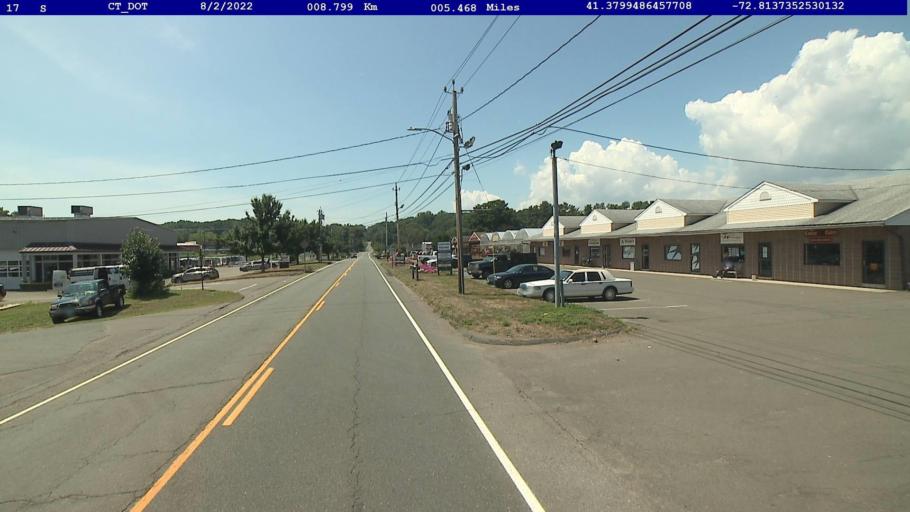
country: US
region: Connecticut
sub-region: New Haven County
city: North Haven
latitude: 41.3793
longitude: -72.8138
